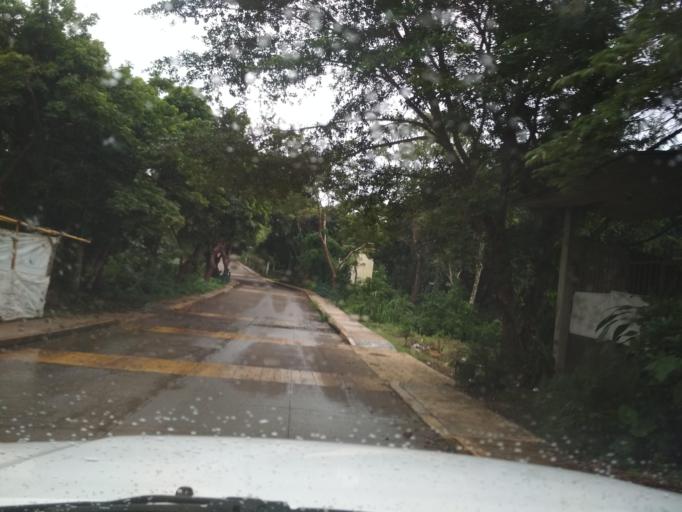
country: MX
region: Veracruz
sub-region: San Andres Tuxtla
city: Tonalapan
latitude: 18.4575
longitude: -95.2275
